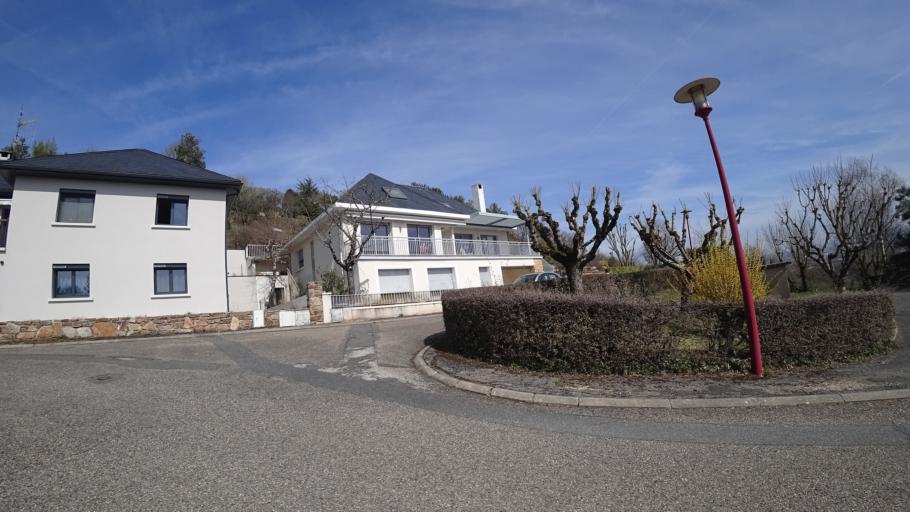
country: FR
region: Midi-Pyrenees
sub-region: Departement de l'Aveyron
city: Rodez
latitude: 44.3700
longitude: 2.5587
